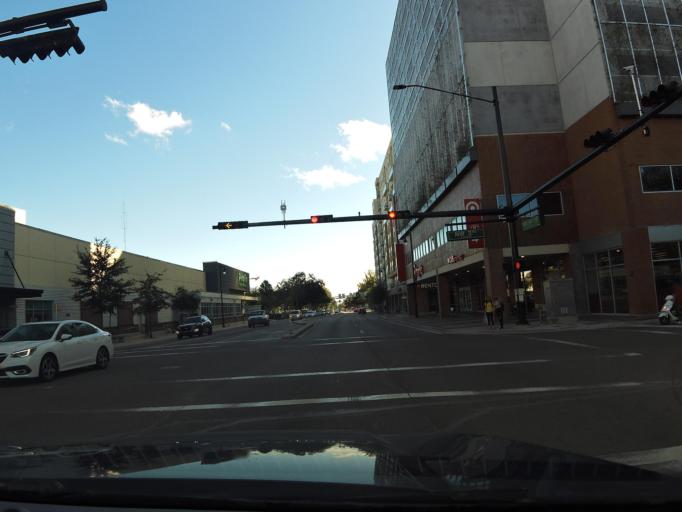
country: US
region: Florida
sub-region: Alachua County
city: Gainesville
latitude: 29.6540
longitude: -82.3393
